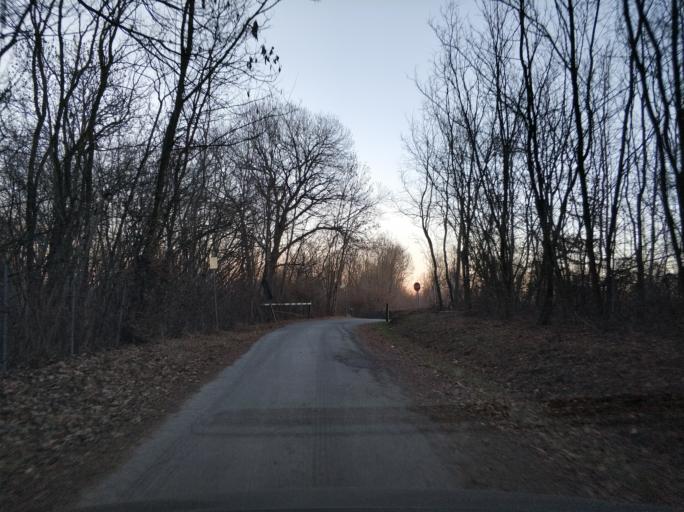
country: IT
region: Piedmont
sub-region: Provincia di Torino
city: Vauda Canavese Superiore
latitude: 45.2665
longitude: 7.6197
